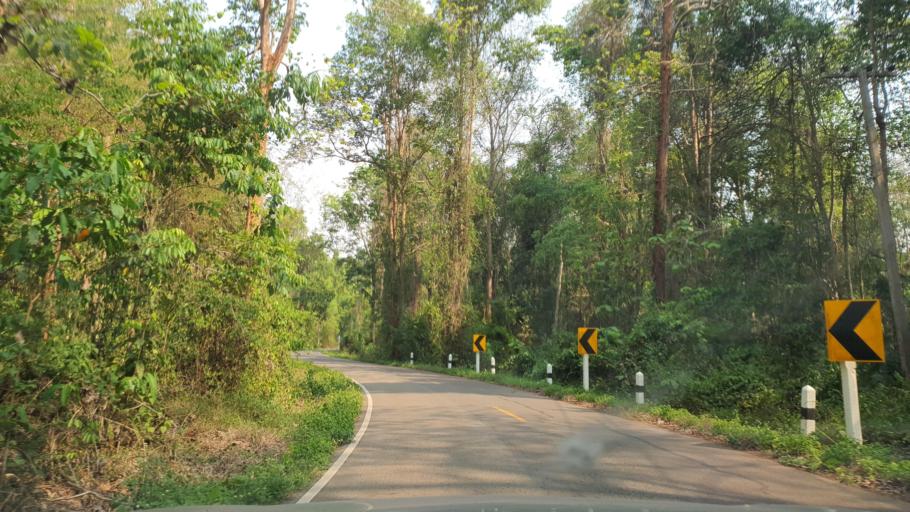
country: TH
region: Chiang Mai
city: San Sai
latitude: 19.0035
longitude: 99.1253
